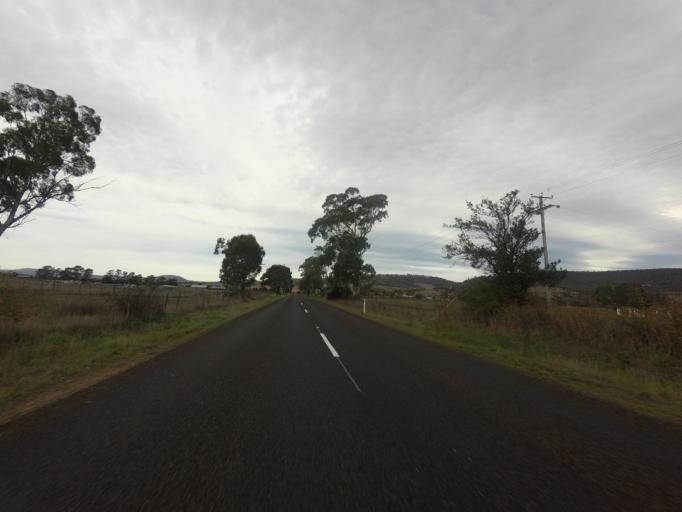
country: AU
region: Tasmania
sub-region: Brighton
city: Bridgewater
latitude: -42.6871
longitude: 147.1877
